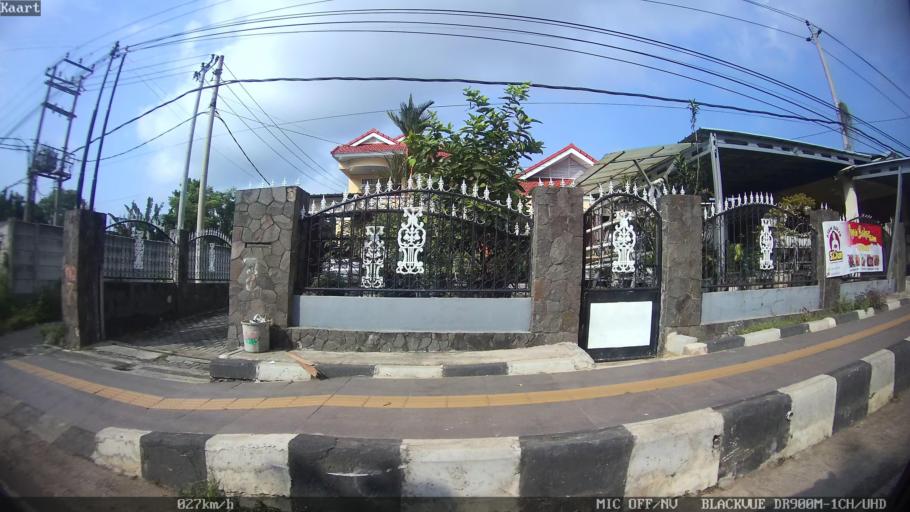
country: ID
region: Lampung
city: Bandarlampung
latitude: -5.4333
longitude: 105.2494
